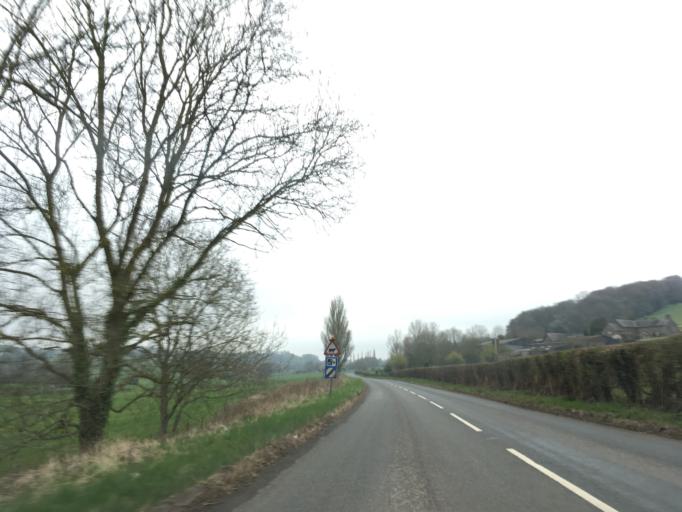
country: GB
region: Wales
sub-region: Newport
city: Caerleon
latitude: 51.6344
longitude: -2.9412
